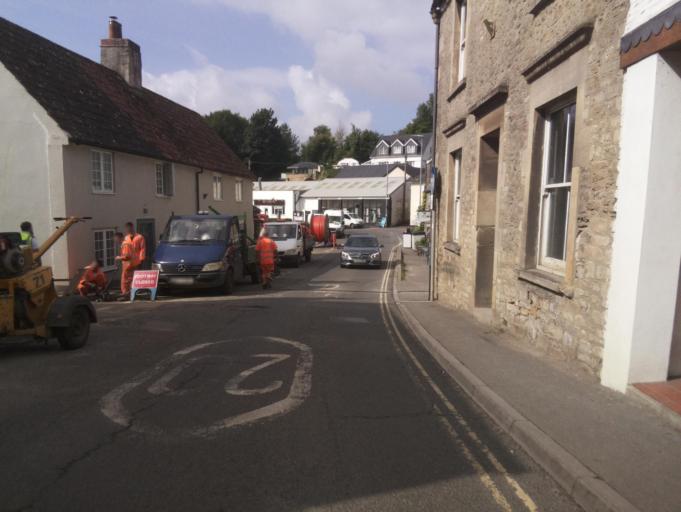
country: GB
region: England
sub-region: Somerset
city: Bruton
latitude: 51.1105
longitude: -2.4583
